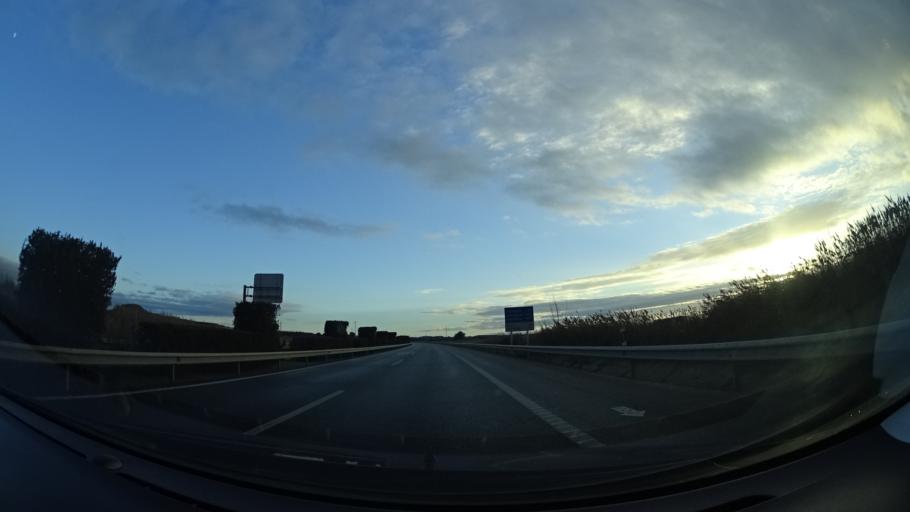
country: ES
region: Catalonia
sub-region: Provincia de Lleida
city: Lleida
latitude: 41.5733
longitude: 0.6224
